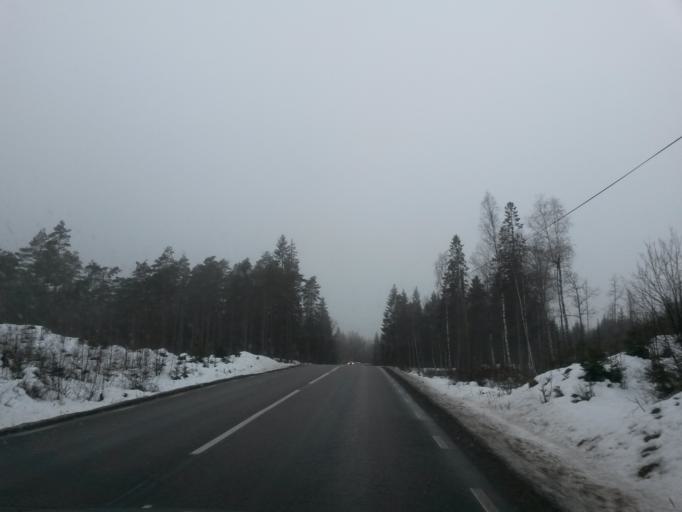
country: SE
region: Vaestra Goetaland
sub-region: Boras Kommun
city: Dalsjofors
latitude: 57.6939
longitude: 13.0959
